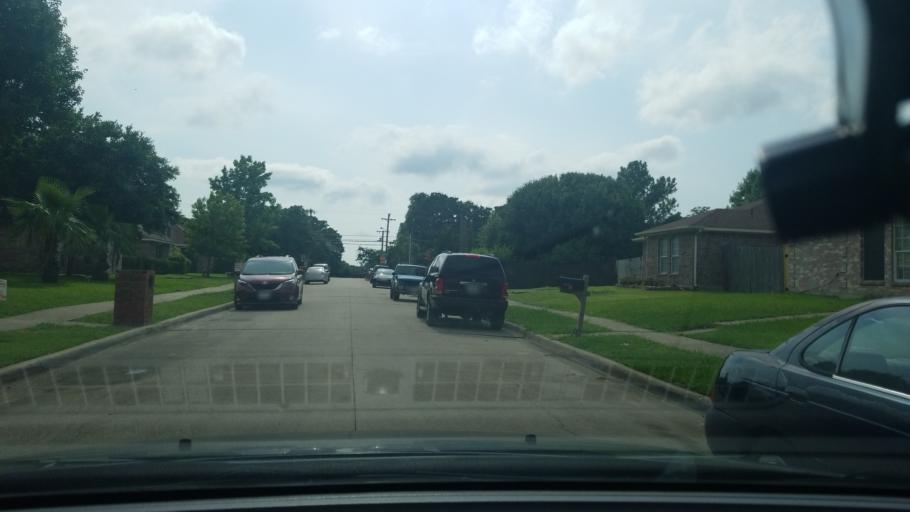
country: US
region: Texas
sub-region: Dallas County
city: Balch Springs
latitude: 32.7575
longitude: -96.6299
